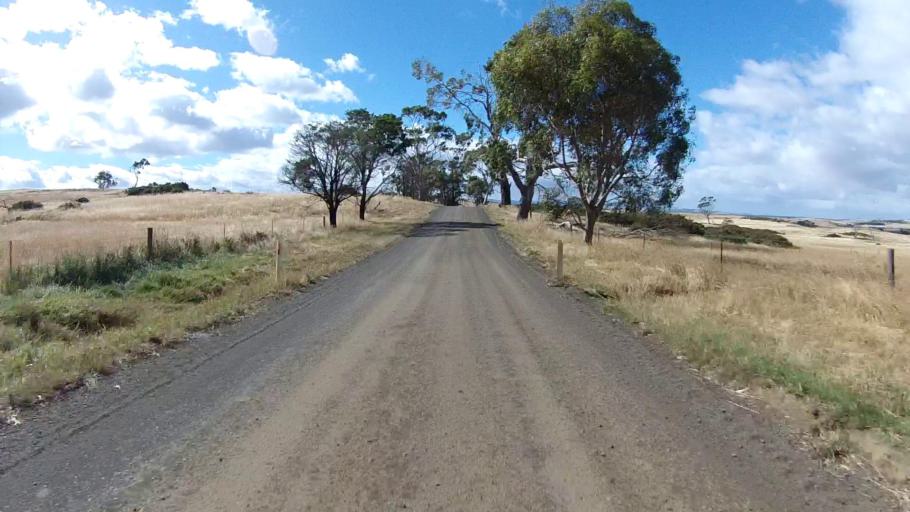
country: AU
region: Tasmania
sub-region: Northern Midlands
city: Evandale
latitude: -41.7186
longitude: 147.4231
